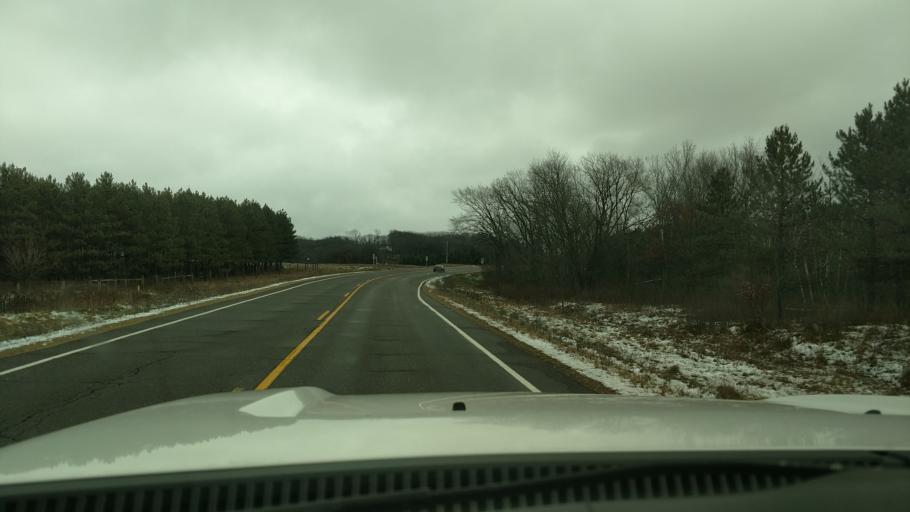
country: US
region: Wisconsin
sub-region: Dunn County
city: Boyceville
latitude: 45.1362
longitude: -91.9336
